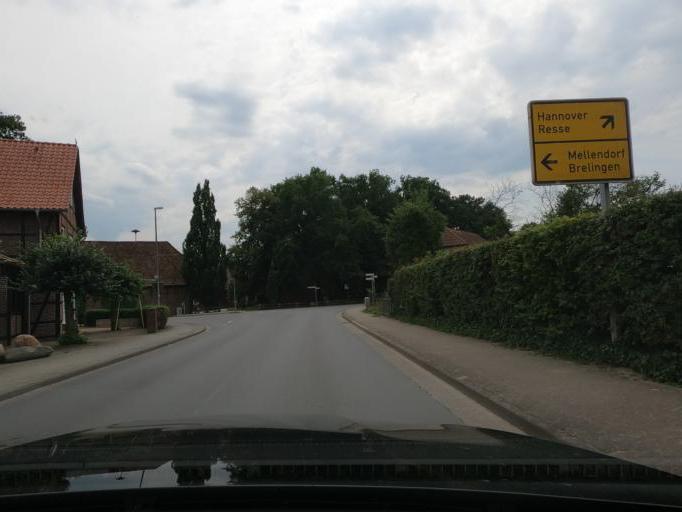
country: DE
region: Lower Saxony
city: Lindwedel
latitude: 52.5536
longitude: 9.6322
